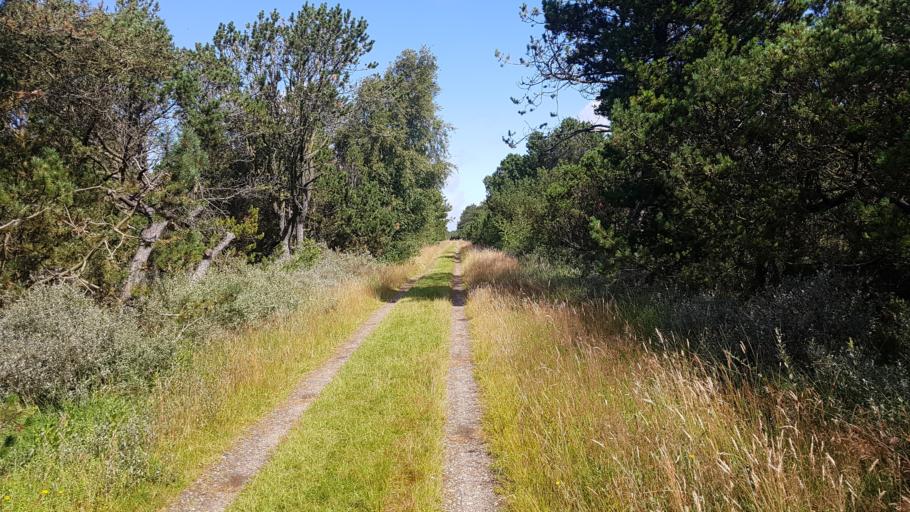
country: DE
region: Schleswig-Holstein
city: List
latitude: 55.1188
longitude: 8.5384
